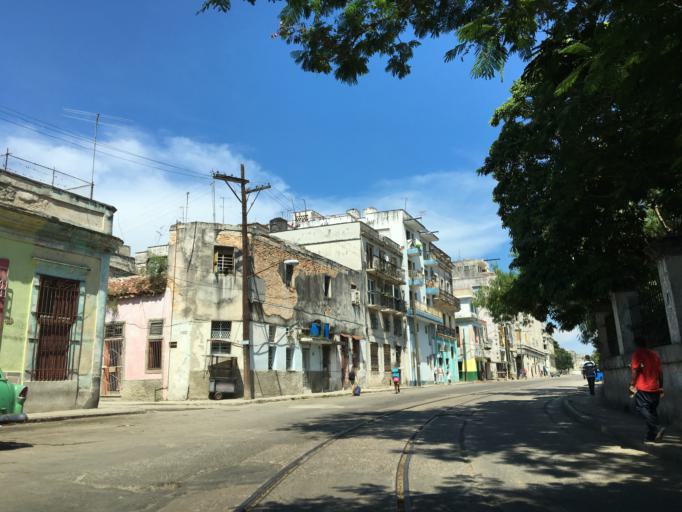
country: CU
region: La Habana
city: La Habana Vieja
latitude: 23.1290
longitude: -82.3575
